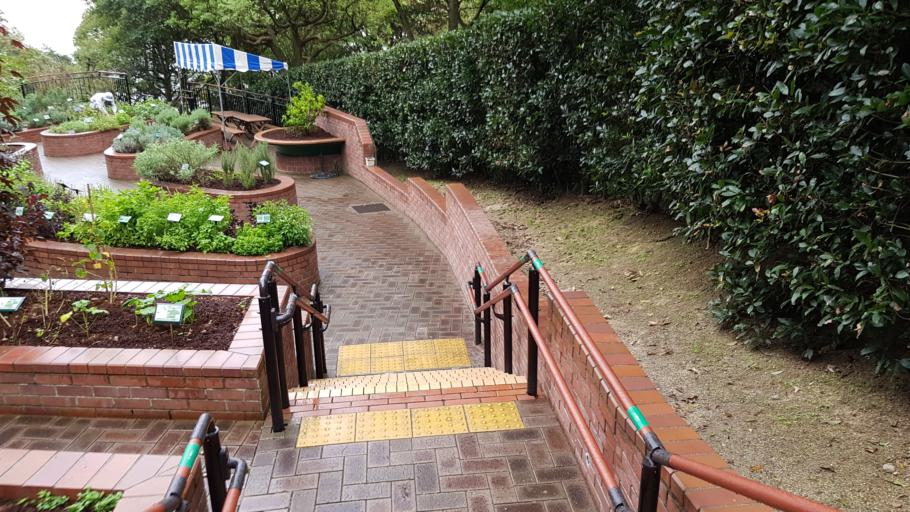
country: JP
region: Hyogo
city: Kobe
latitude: 34.7166
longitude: 135.1917
